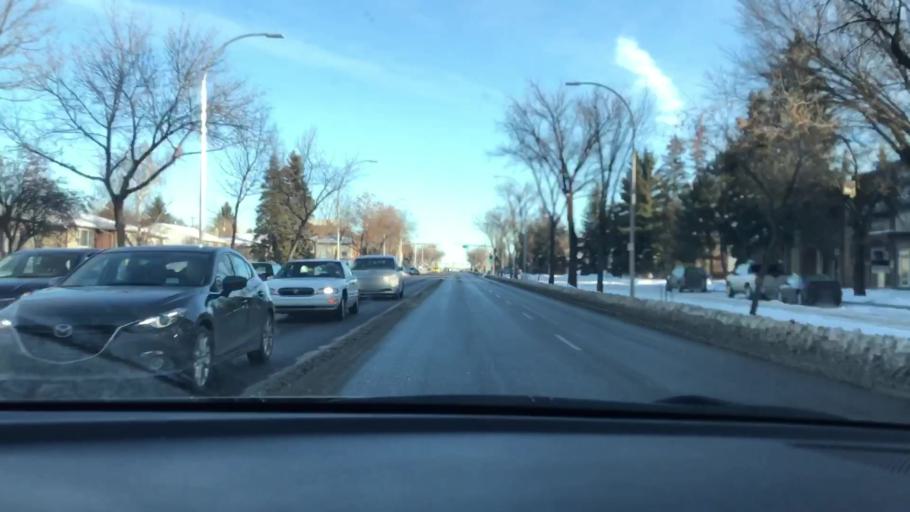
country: CA
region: Alberta
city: Edmonton
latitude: 53.5181
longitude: -113.4516
